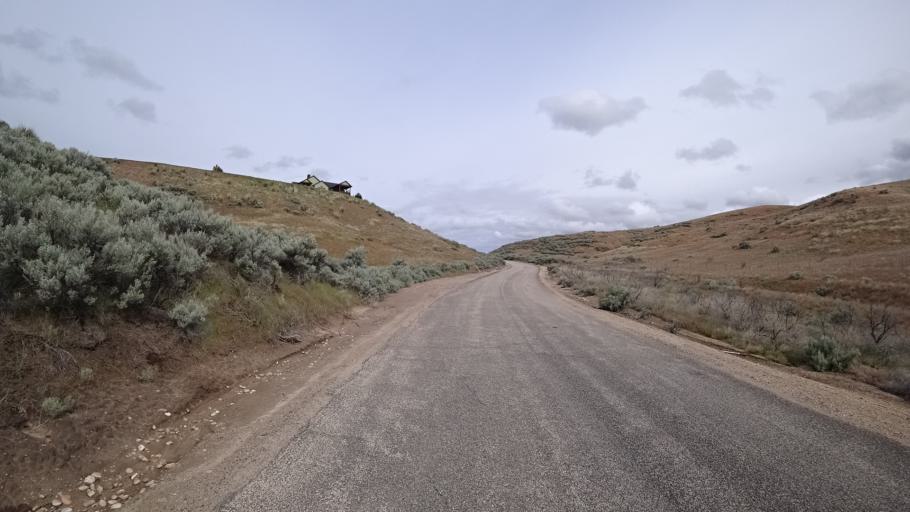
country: US
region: Idaho
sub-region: Ada County
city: Eagle
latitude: 43.7572
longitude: -116.3671
